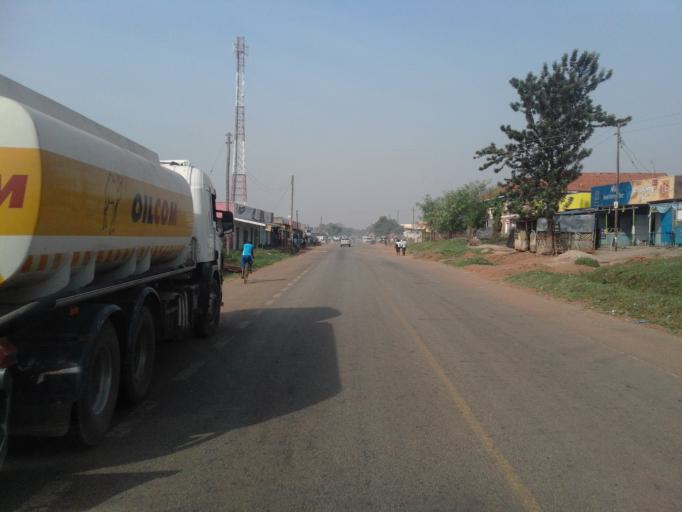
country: UG
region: Eastern Region
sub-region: Budaka District
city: Budaka
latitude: 1.0163
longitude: 33.9510
